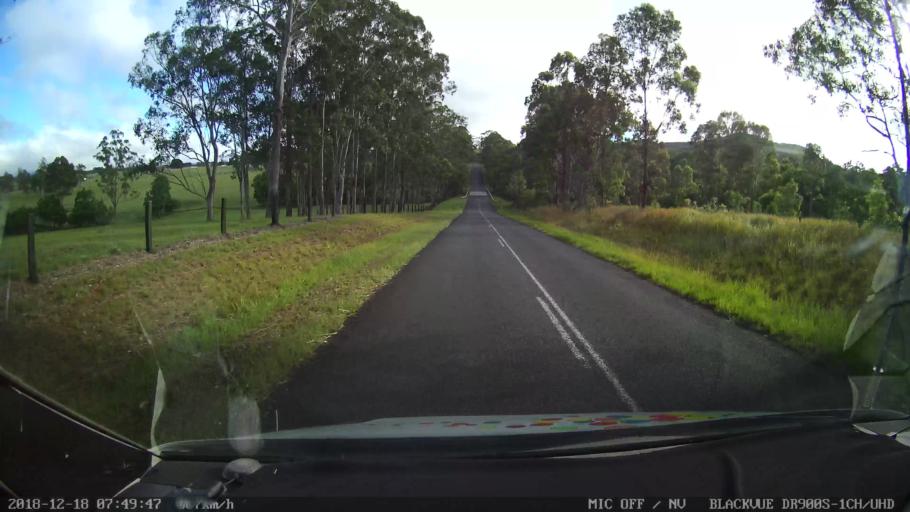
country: AU
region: New South Wales
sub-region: Kyogle
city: Kyogle
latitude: -28.4510
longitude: 152.5710
